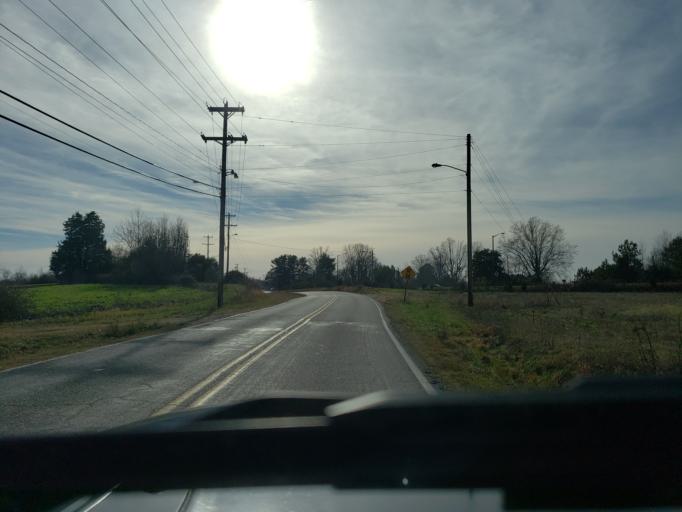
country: US
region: North Carolina
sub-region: Cleveland County
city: Kings Mountain
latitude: 35.2251
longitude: -81.3320
